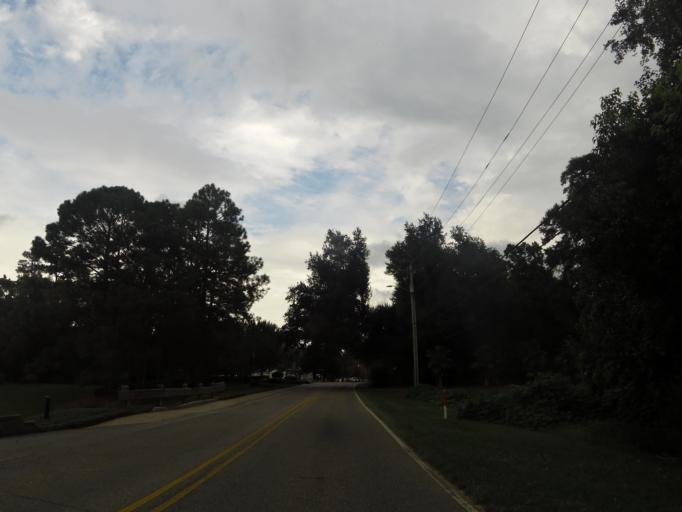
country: US
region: Alabama
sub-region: Baldwin County
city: Fairhope
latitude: 30.5116
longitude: -87.9187
